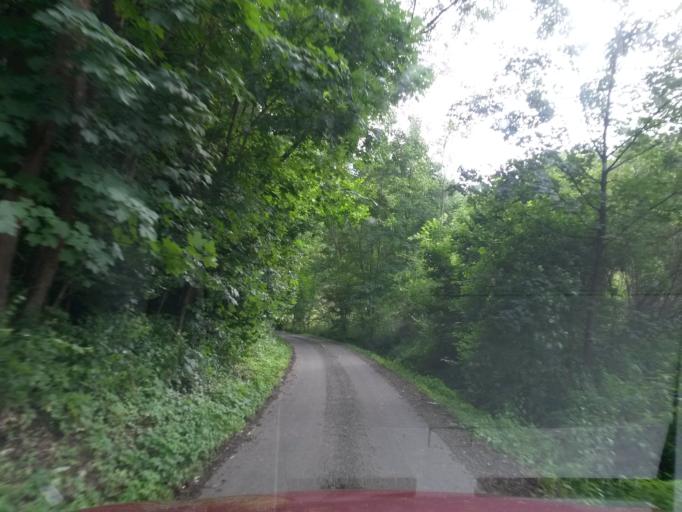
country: SK
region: Banskobystricky
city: Detva
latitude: 48.4862
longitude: 19.2934
